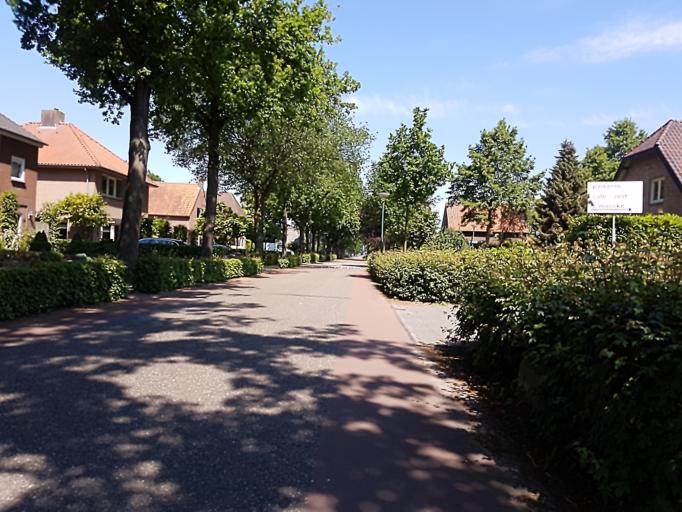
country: NL
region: North Brabant
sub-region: Gemeente Loon op Zand
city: Loon op Zand
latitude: 51.6249
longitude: 5.0135
